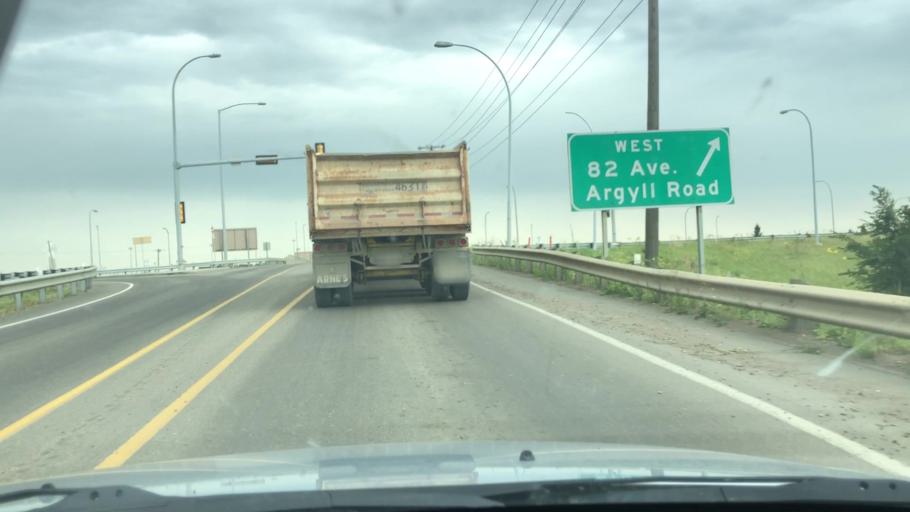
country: CA
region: Alberta
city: Sherwood Park
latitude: 53.5183
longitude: -113.3939
